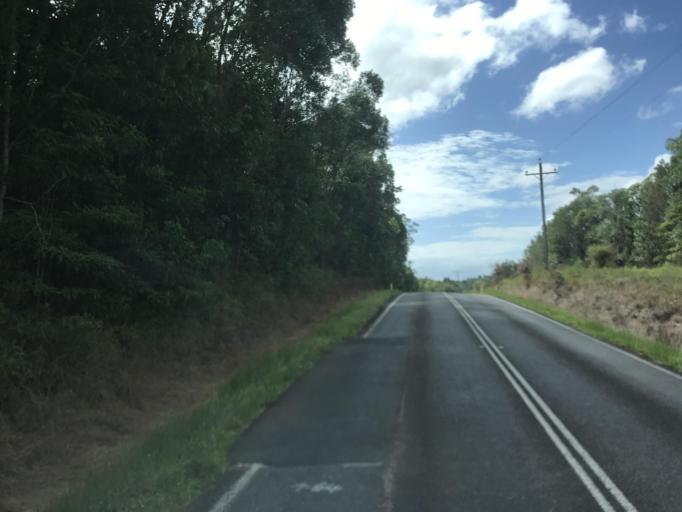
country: AU
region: Queensland
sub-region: Cassowary Coast
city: Innisfail
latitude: -17.8425
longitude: 146.0551
